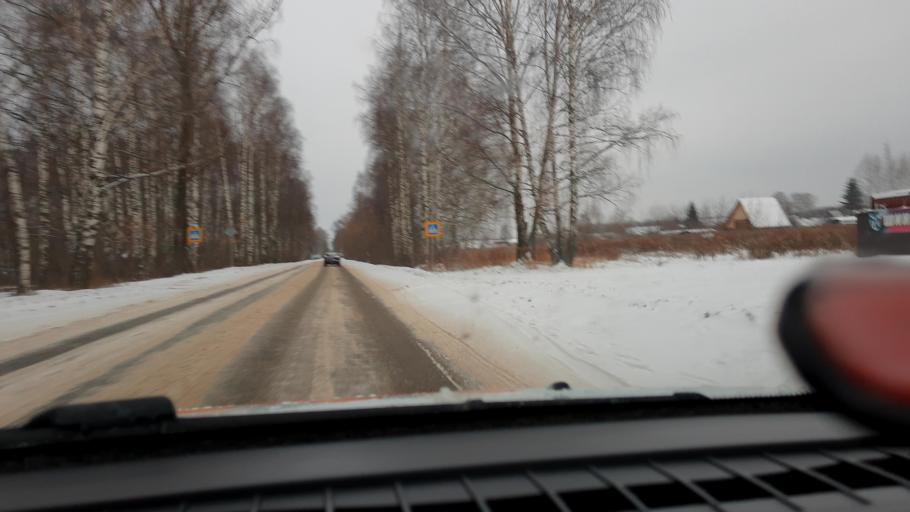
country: RU
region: Nizjnij Novgorod
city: Pamyat' Parizhskoy Kommuny
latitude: 56.2705
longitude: 44.4177
